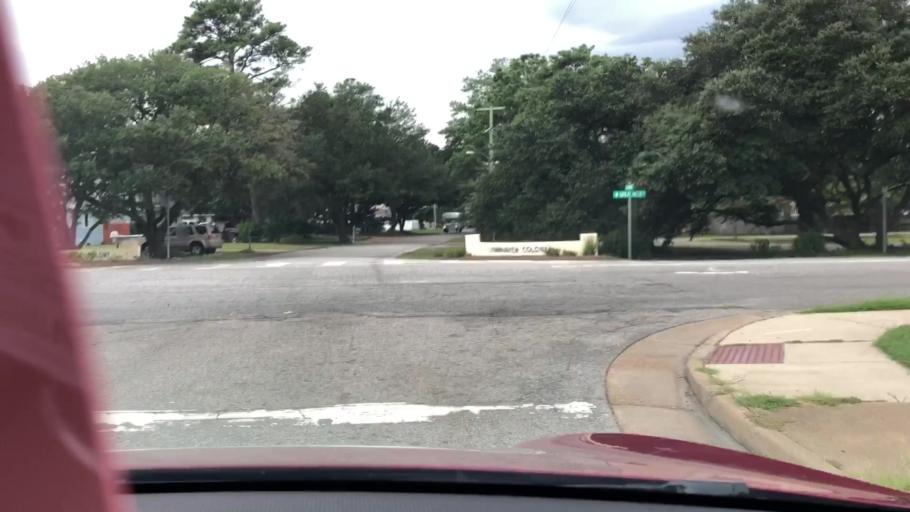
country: US
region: Virginia
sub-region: City of Virginia Beach
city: Virginia Beach
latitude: 36.9075
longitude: -76.0702
